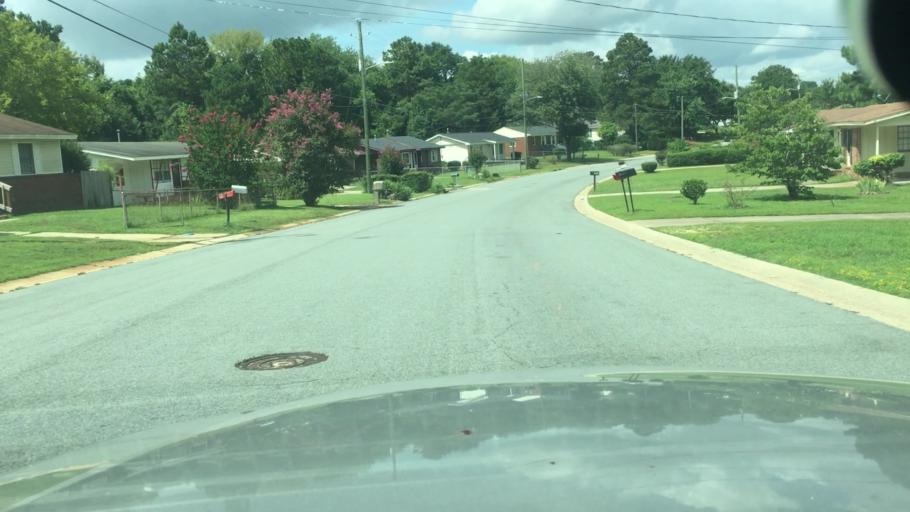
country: US
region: North Carolina
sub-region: Cumberland County
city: Fayetteville
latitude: 35.0260
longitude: -78.9181
